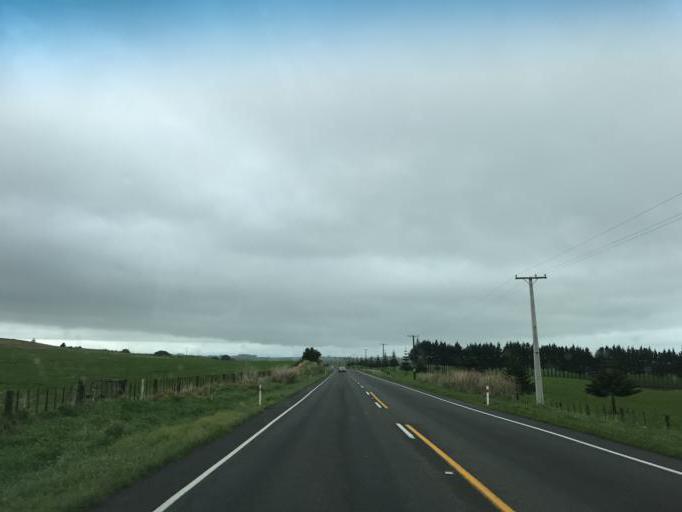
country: NZ
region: Manawatu-Wanganui
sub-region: Wanganui District
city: Wanganui
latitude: -39.8145
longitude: 174.8025
